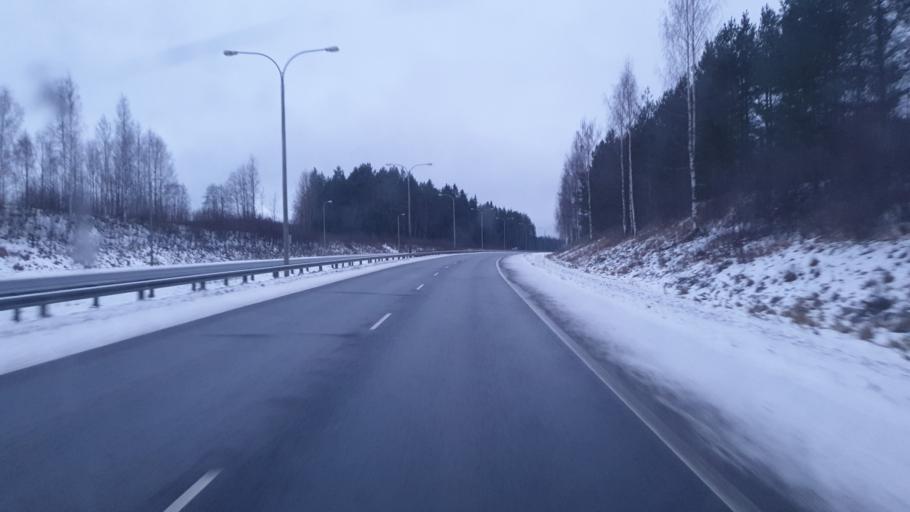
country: FI
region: Northern Savo
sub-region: Kuopio
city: Siilinjaervi
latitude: 63.0560
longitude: 27.6712
